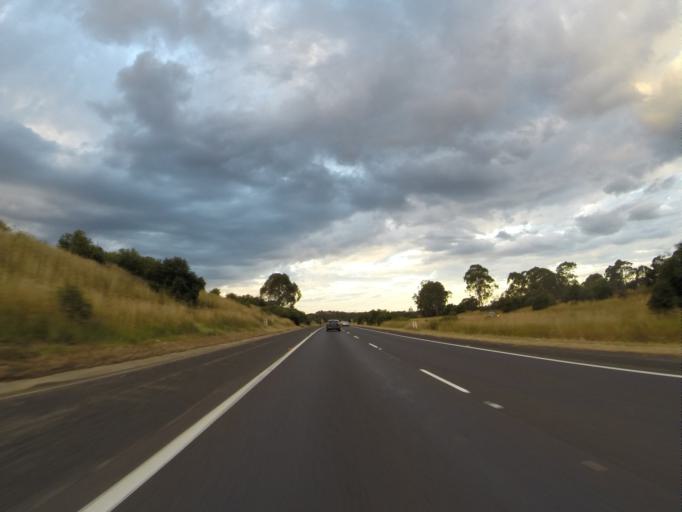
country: AU
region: New South Wales
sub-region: Wollondilly
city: Douglas Park
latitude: -34.1823
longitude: 150.7219
